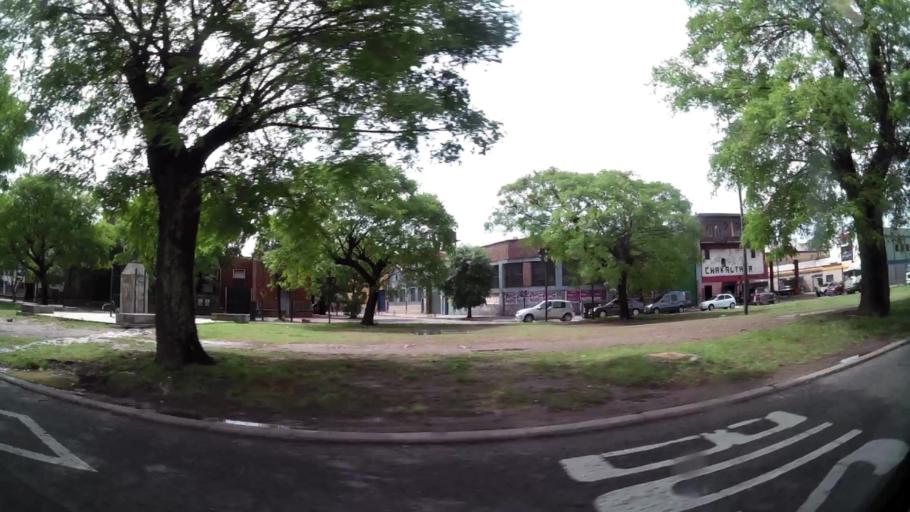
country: AR
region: Buenos Aires
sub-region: Partido de Avellaneda
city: Avellaneda
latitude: -34.6559
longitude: -58.4197
